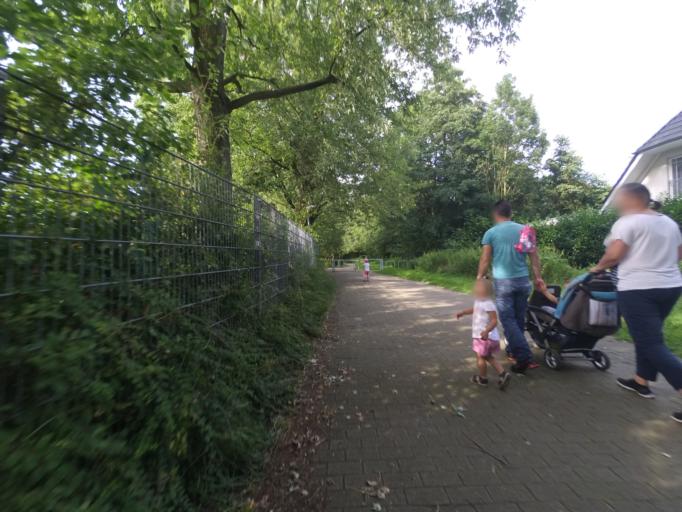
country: DE
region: Hamburg
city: Bergedorf
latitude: 53.4915
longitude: 10.1849
